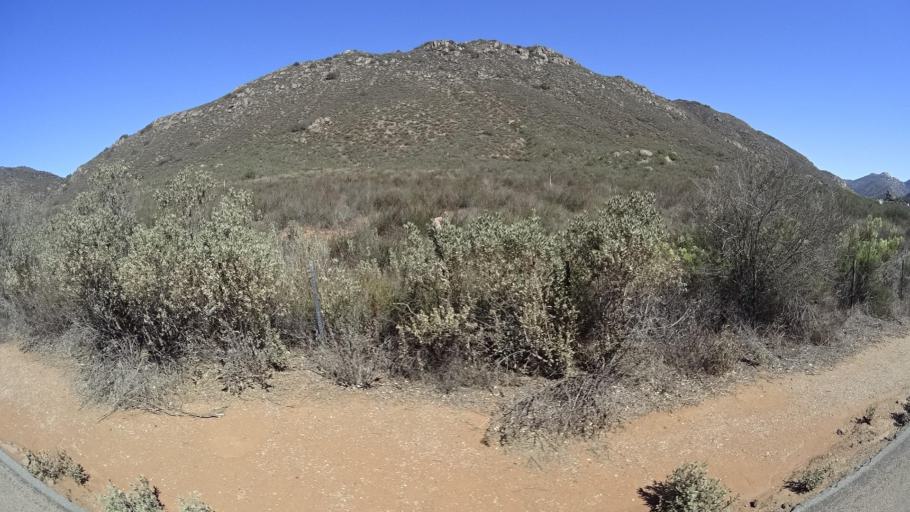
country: US
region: California
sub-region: San Diego County
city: Alpine
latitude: 32.7958
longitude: -116.7456
